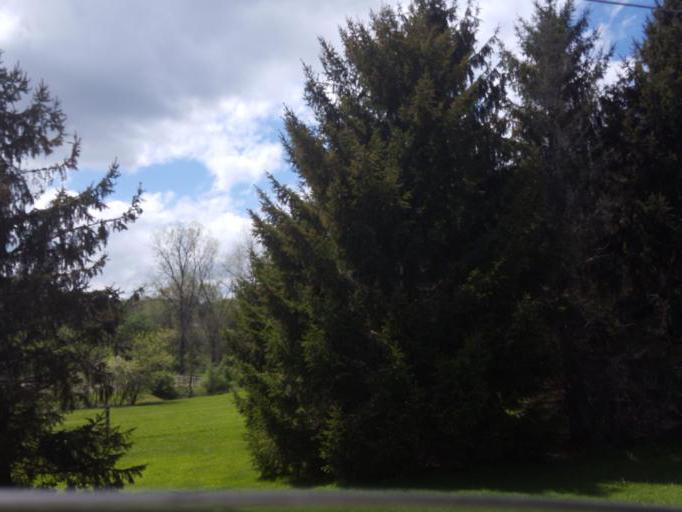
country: US
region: Ohio
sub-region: Richland County
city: Ontario
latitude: 40.7463
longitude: -82.5710
